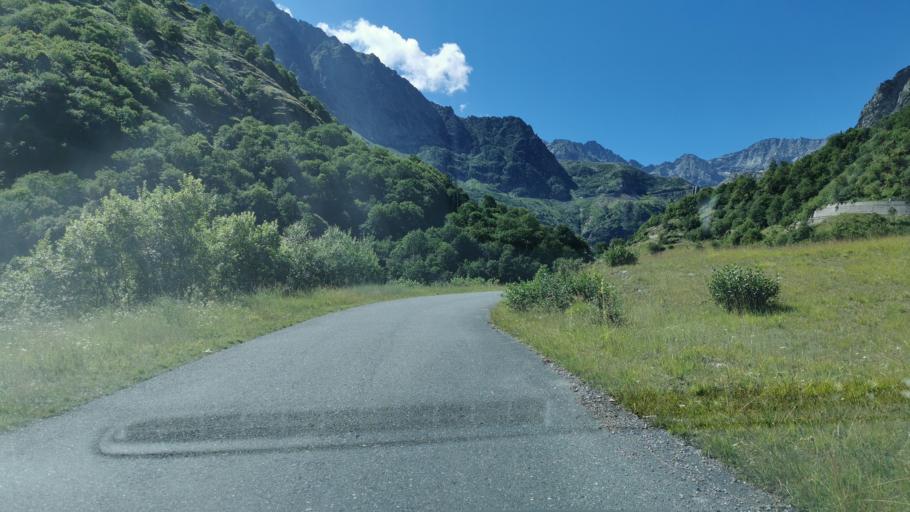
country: IT
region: Piedmont
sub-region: Provincia di Cuneo
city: Entracque
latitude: 44.1866
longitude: 7.3471
